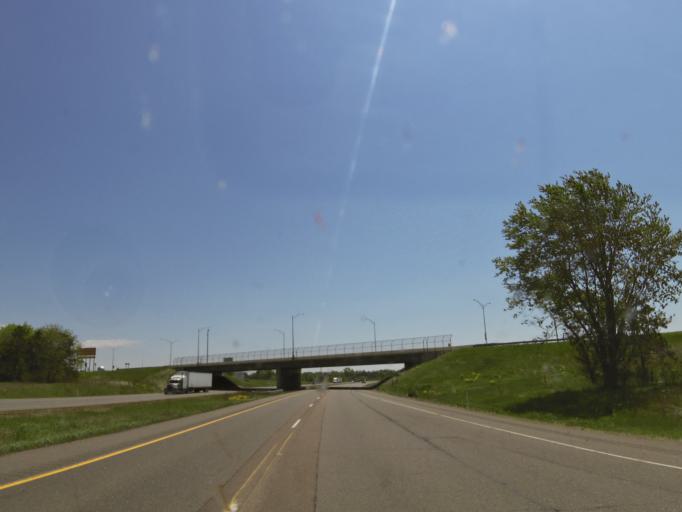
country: US
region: Wisconsin
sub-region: Monroe County
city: Tomah
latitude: 44.0194
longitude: -90.4992
